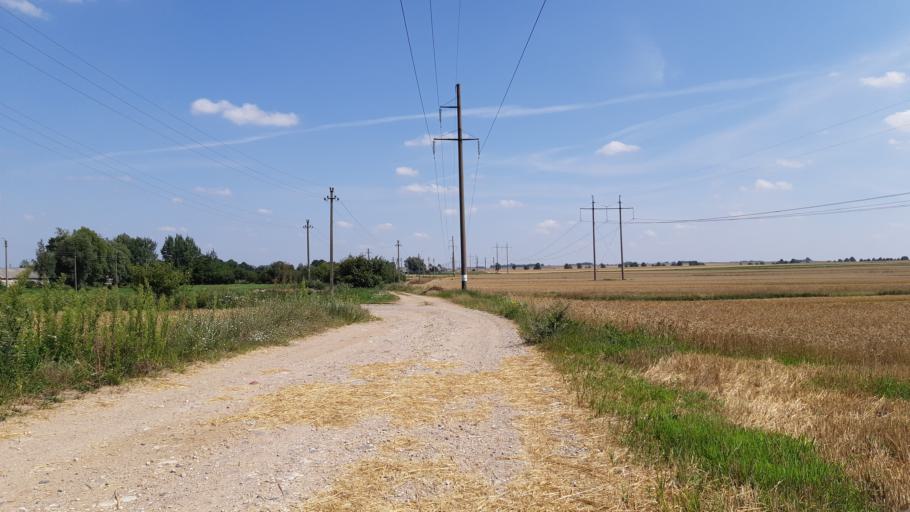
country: LT
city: Virbalis
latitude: 54.6186
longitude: 22.8116
